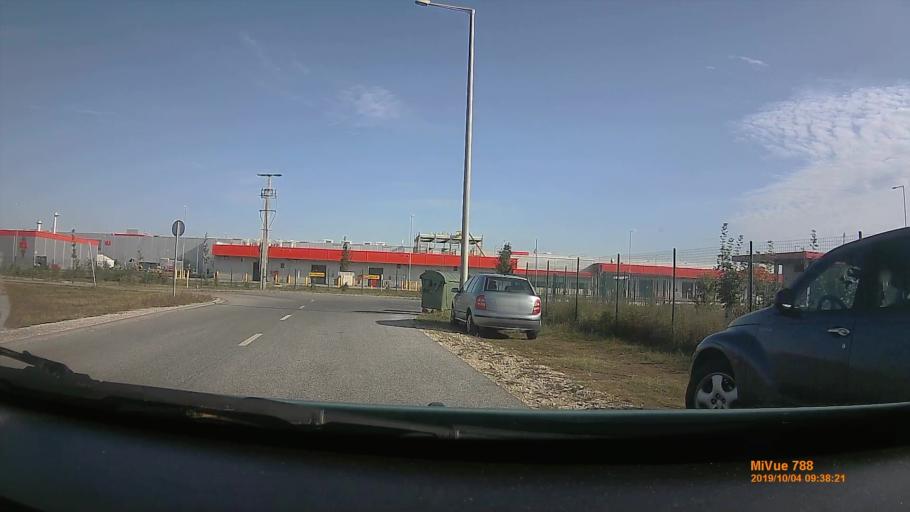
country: HU
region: Szabolcs-Szatmar-Bereg
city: Nyiregyhaza
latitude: 47.9466
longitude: 21.6471
